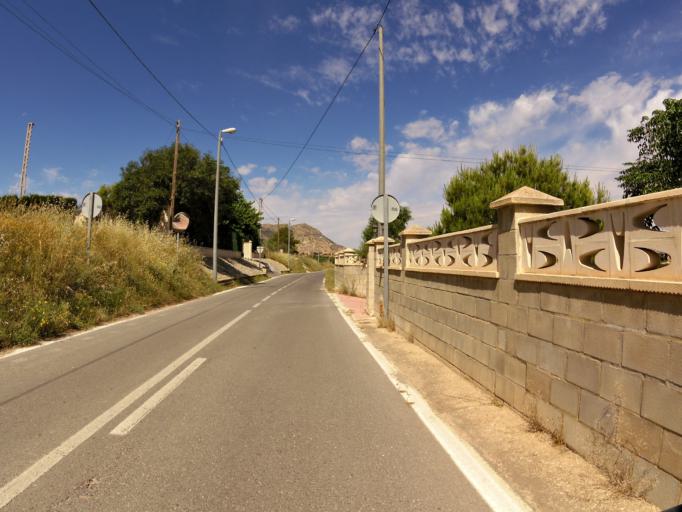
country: ES
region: Valencia
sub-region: Provincia de Alicante
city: Agost
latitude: 38.3951
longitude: -0.5948
